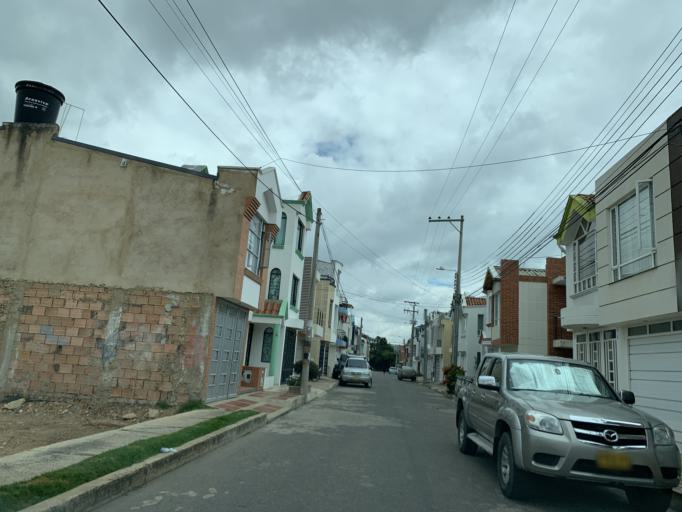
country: CO
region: Boyaca
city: Tunja
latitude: 5.5540
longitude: -73.3470
